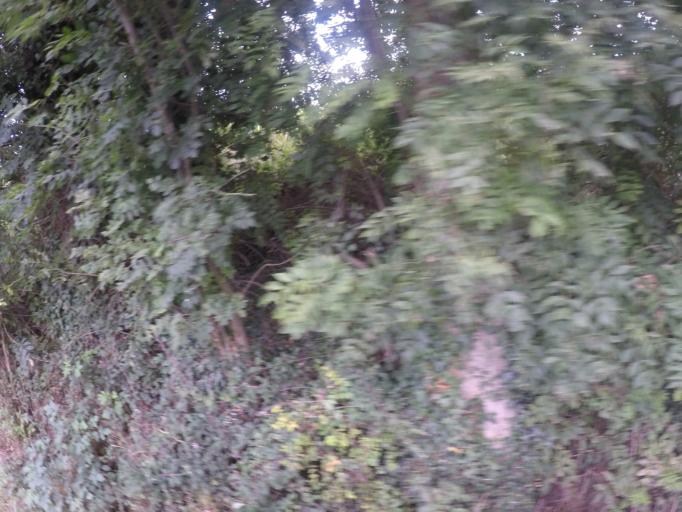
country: FR
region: Brittany
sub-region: Departement des Cotes-d'Armor
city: Lanvollon
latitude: 48.6234
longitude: -2.9916
